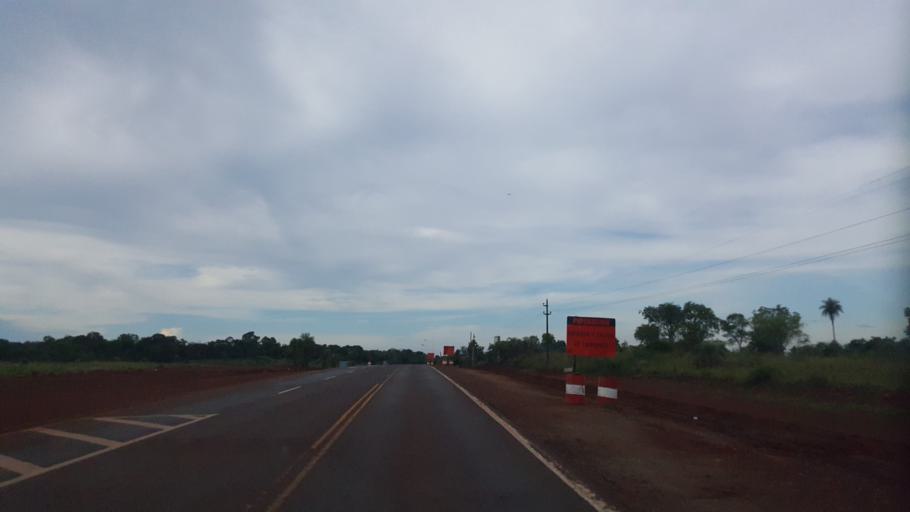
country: AR
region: Misiones
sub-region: Departamento de Candelaria
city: Loreto
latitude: -27.3391
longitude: -55.5450
